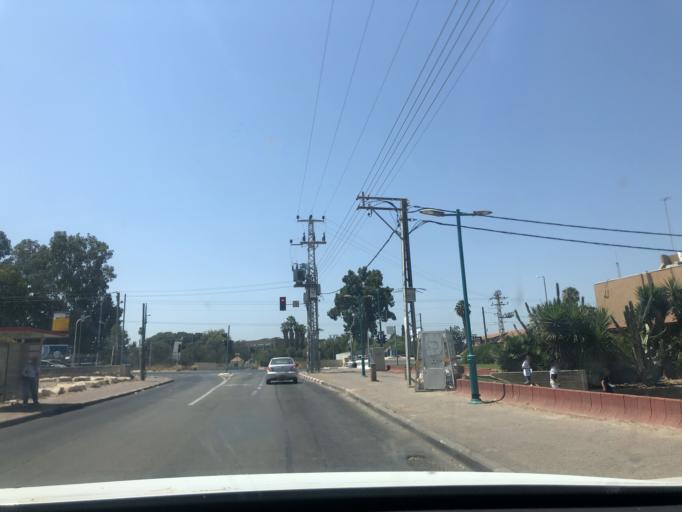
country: IL
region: Central District
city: Lod
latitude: 31.9379
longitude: 34.8866
